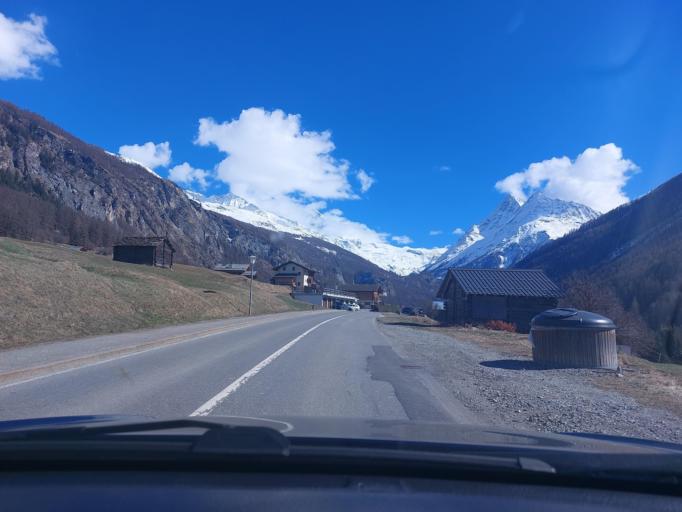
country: CH
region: Valais
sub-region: Herens District
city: Evolene
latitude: 46.1206
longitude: 7.4852
